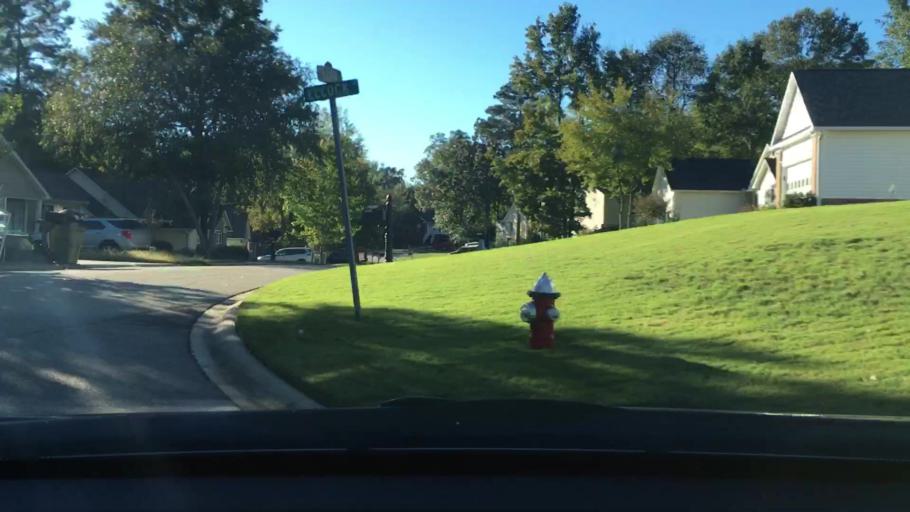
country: US
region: South Carolina
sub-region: Lexington County
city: Irmo
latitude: 34.1170
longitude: -81.1754
